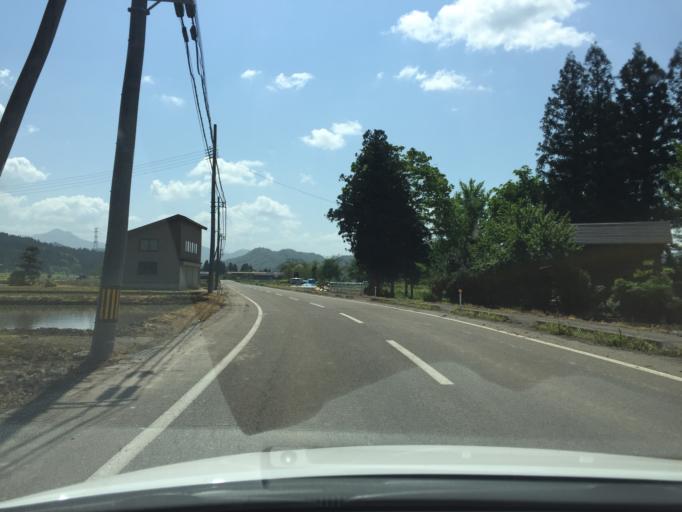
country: JP
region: Niigata
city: Tochio-honcho
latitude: 37.5528
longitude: 139.0798
